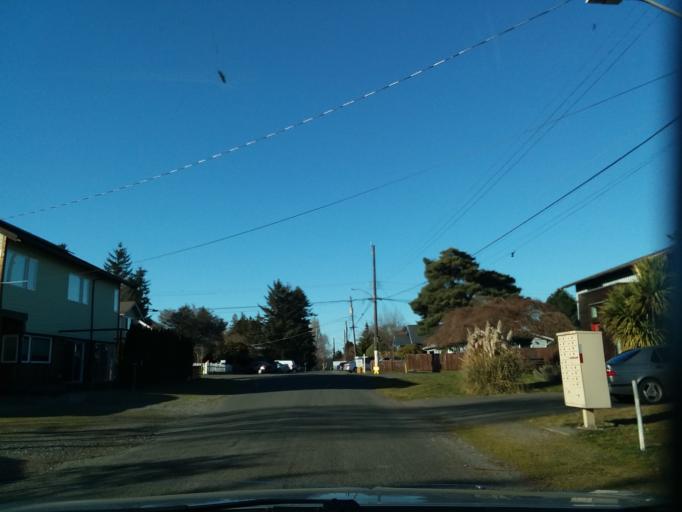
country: US
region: Washington
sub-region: King County
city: Shoreline
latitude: 47.6924
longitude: -122.3673
